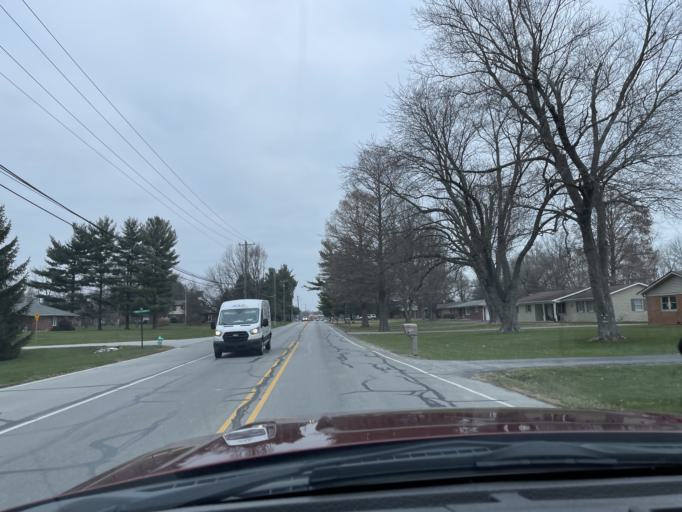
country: US
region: Indiana
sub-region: Hendricks County
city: Avon
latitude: 39.7732
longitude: -86.3996
